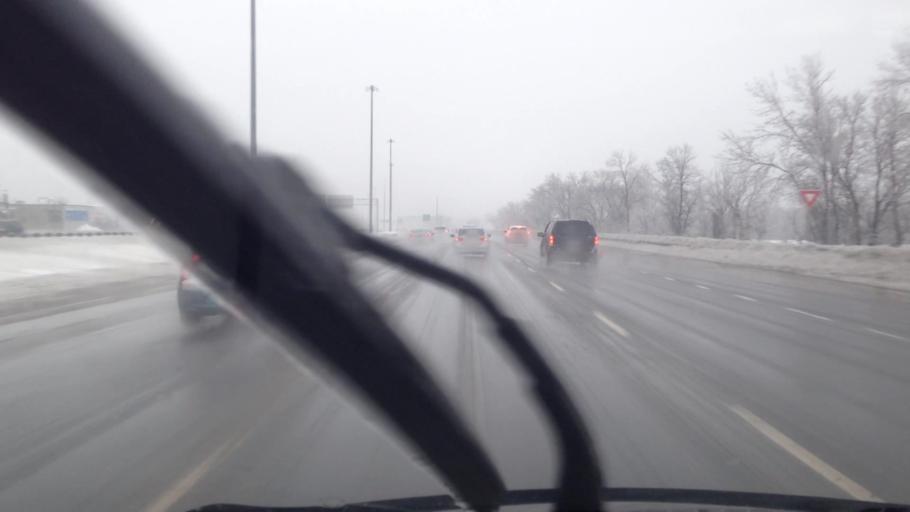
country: CA
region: Quebec
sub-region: Laurentides
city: Boisbriand
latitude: 45.6236
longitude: -73.8354
